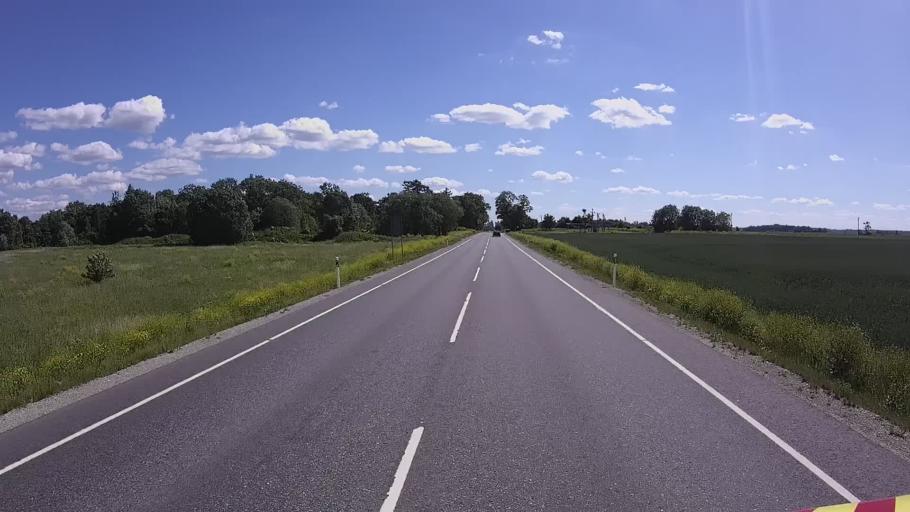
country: EE
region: Ida-Virumaa
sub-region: Johvi vald
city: Johvi
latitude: 59.3562
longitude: 27.3508
